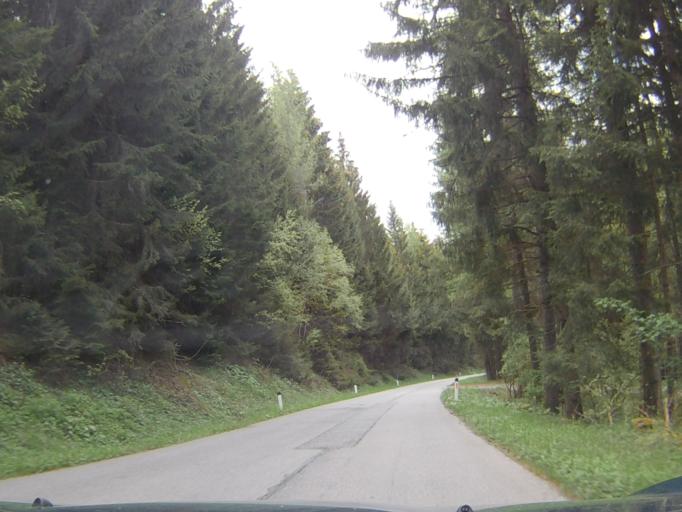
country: AT
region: Carinthia
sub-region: Politischer Bezirk Villach Land
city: Stockenboi
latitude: 46.7360
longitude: 13.5648
